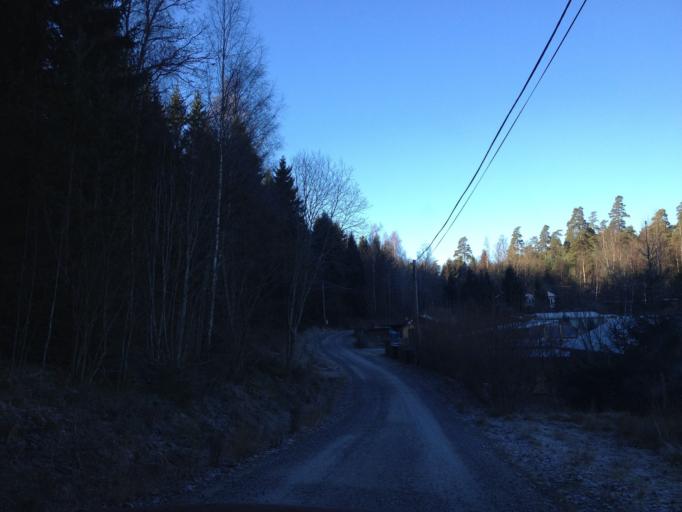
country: SE
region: Stockholm
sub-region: Sodertalje Kommun
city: Soedertaelje
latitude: 59.1624
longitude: 17.5813
